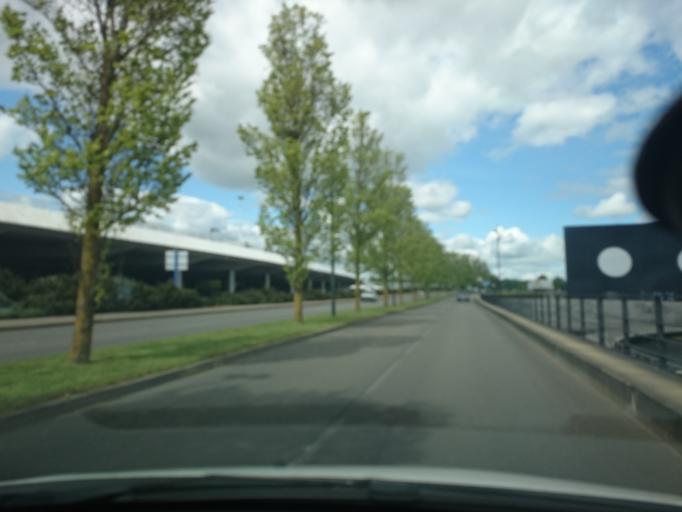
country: FR
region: Pays de la Loire
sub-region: Departement de la Loire-Atlantique
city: Saint-Herblain
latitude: 47.2228
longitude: -1.6301
